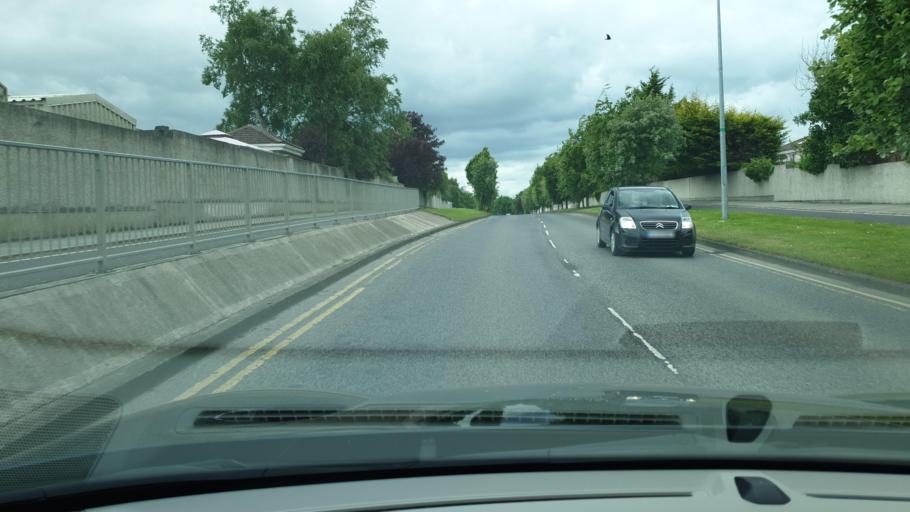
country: IE
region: Leinster
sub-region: An Mhi
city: Ratoath
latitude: 53.5031
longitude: -6.4612
